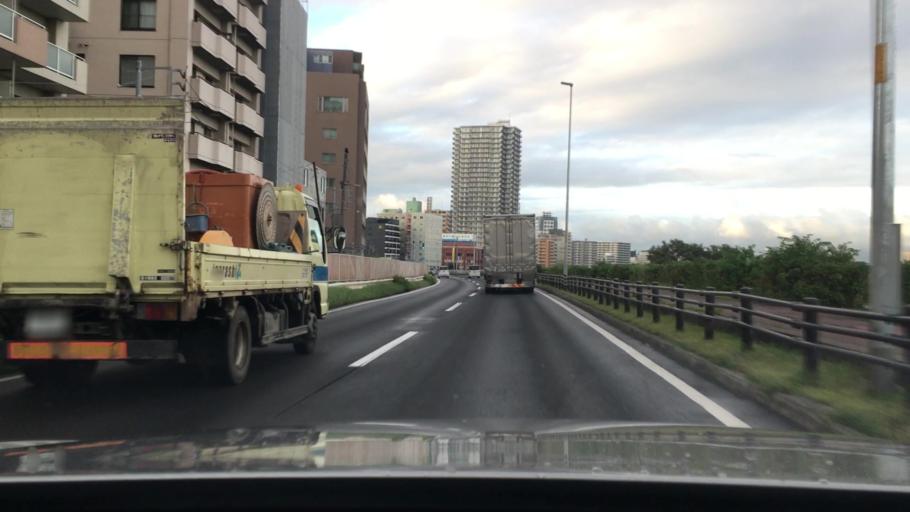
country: JP
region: Hokkaido
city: Sapporo
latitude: 43.0447
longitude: 141.3582
